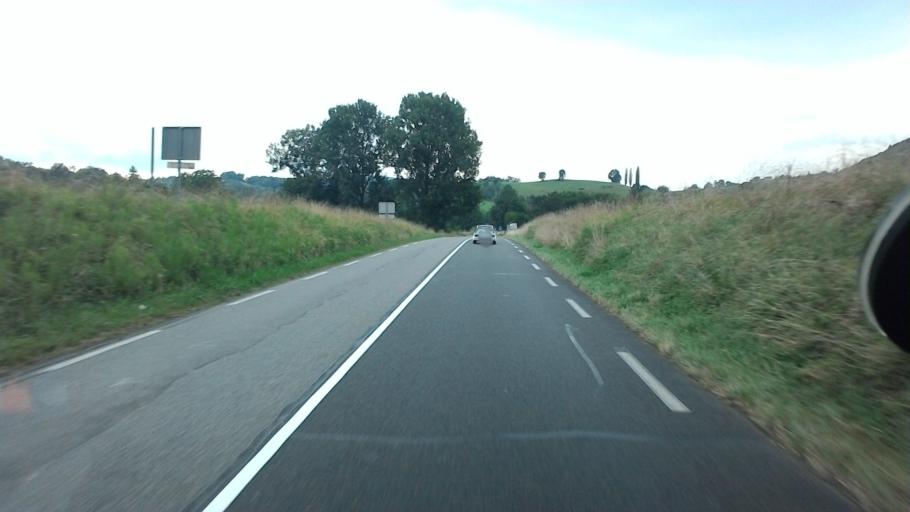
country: FR
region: Rhone-Alpes
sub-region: Departement de la Savoie
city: Yenne
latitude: 45.6930
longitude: 5.8099
